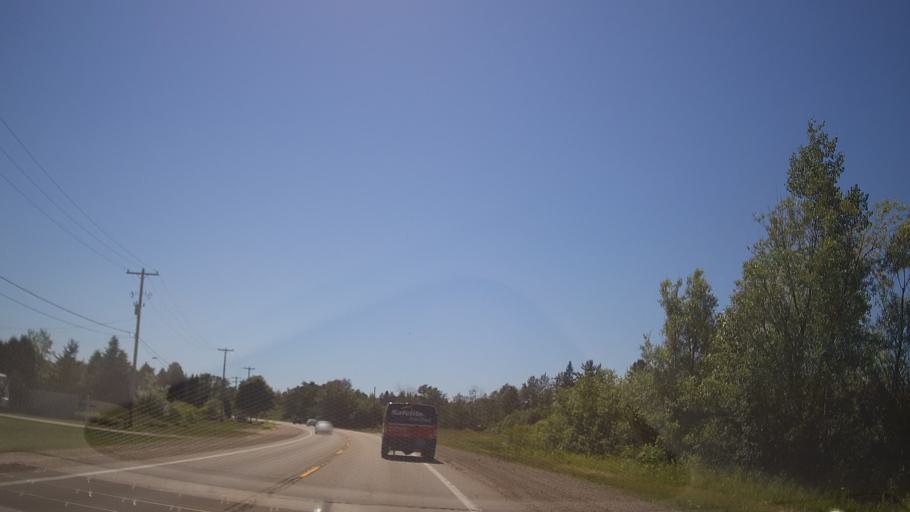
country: US
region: Michigan
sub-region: Emmet County
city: Petoskey
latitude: 45.4240
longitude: -84.8569
